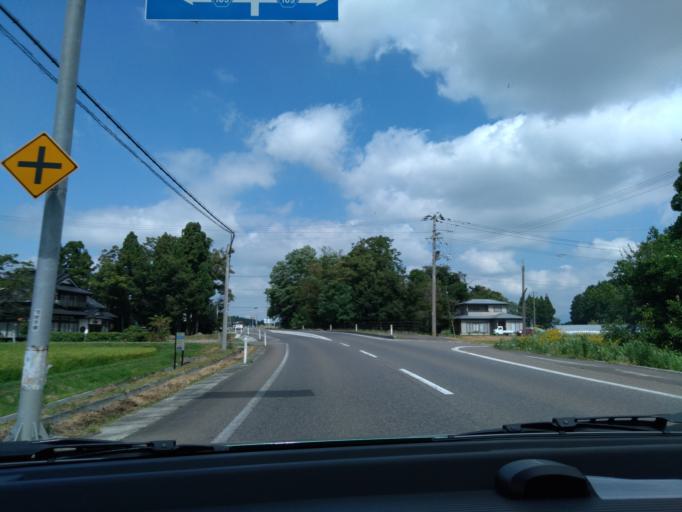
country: JP
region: Iwate
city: Hanamaki
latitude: 39.4589
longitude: 141.1010
